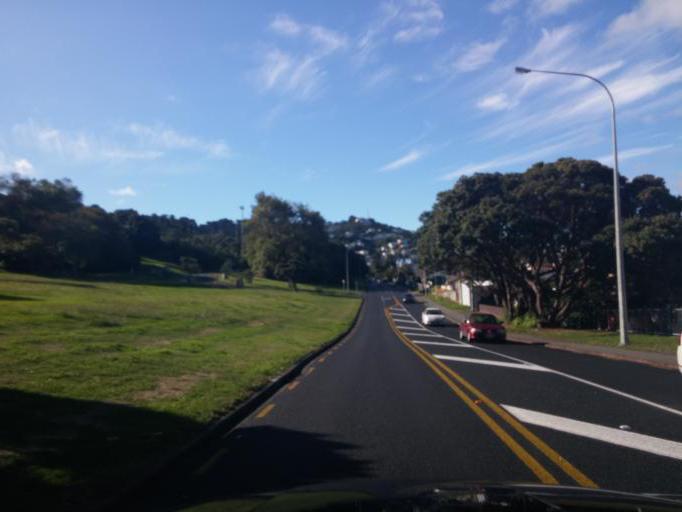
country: NZ
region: Wellington
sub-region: Wellington City
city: Wellington
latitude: -41.3097
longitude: 174.7912
